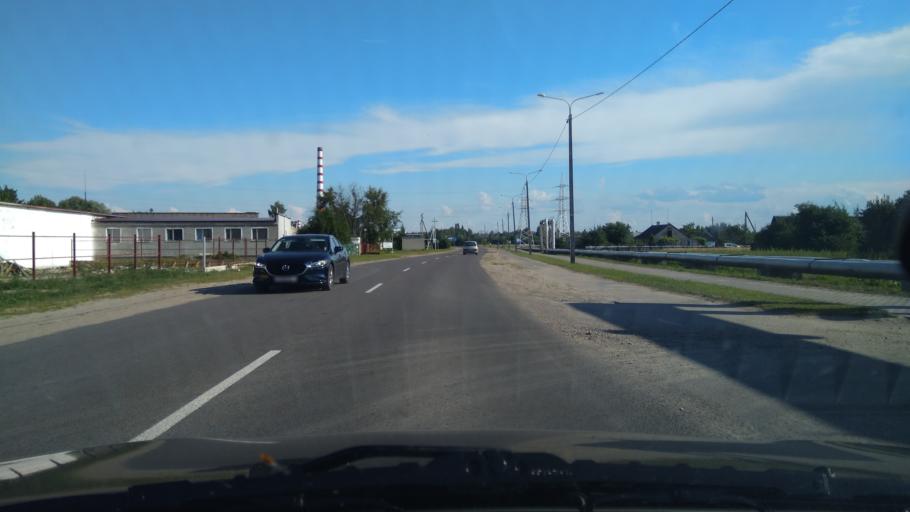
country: BY
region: Brest
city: Byelaazyorsk
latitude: 52.4652
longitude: 25.1867
